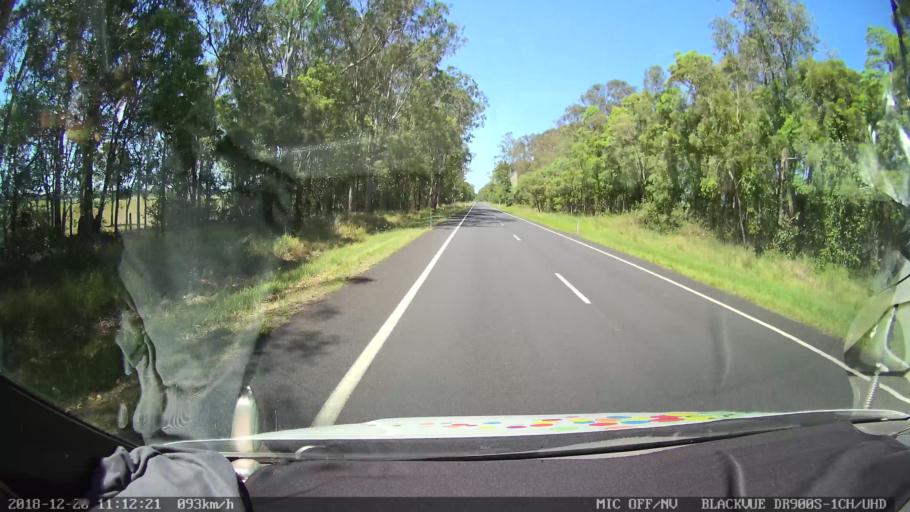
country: AU
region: New South Wales
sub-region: Richmond Valley
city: Casino
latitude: -28.9728
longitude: 153.0112
